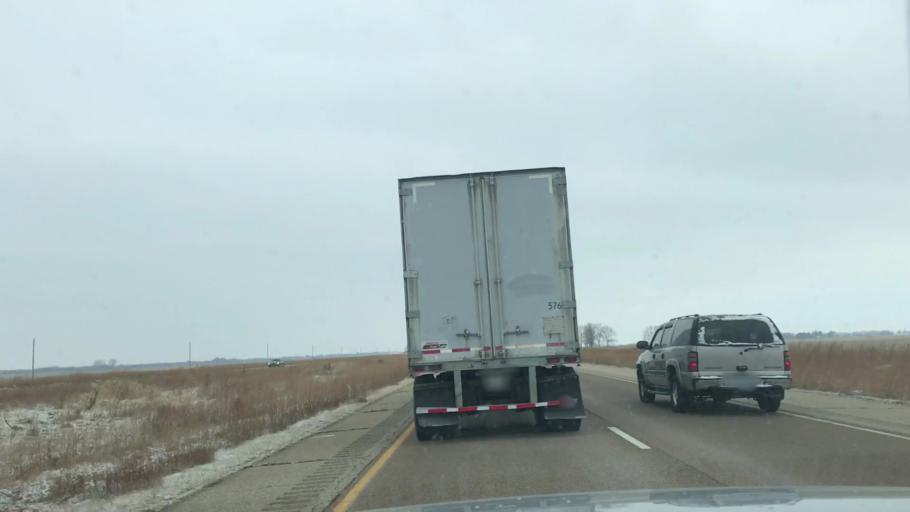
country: US
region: Illinois
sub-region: Montgomery County
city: Raymond
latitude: 39.3880
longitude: -89.6429
